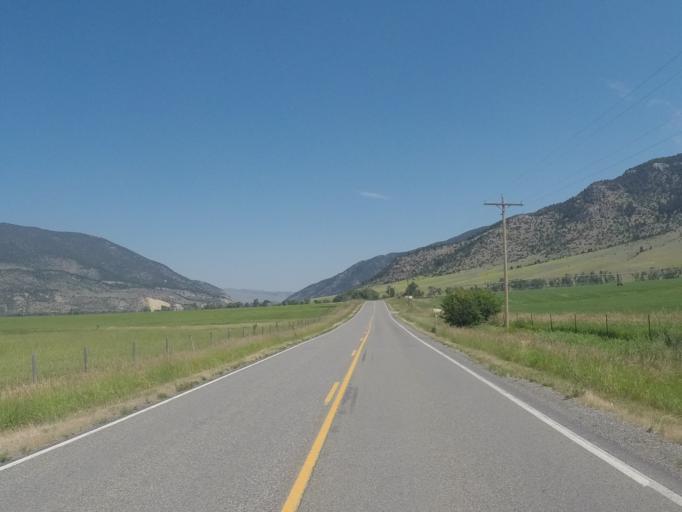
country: US
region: Montana
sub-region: Park County
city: Livingston
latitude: 45.5606
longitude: -110.5589
